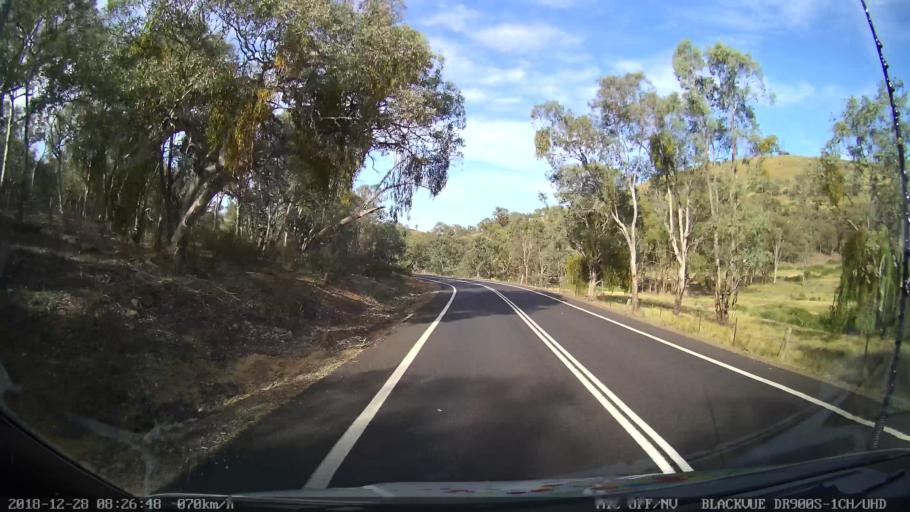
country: AU
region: New South Wales
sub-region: Blayney
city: Blayney
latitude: -33.9386
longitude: 149.3437
